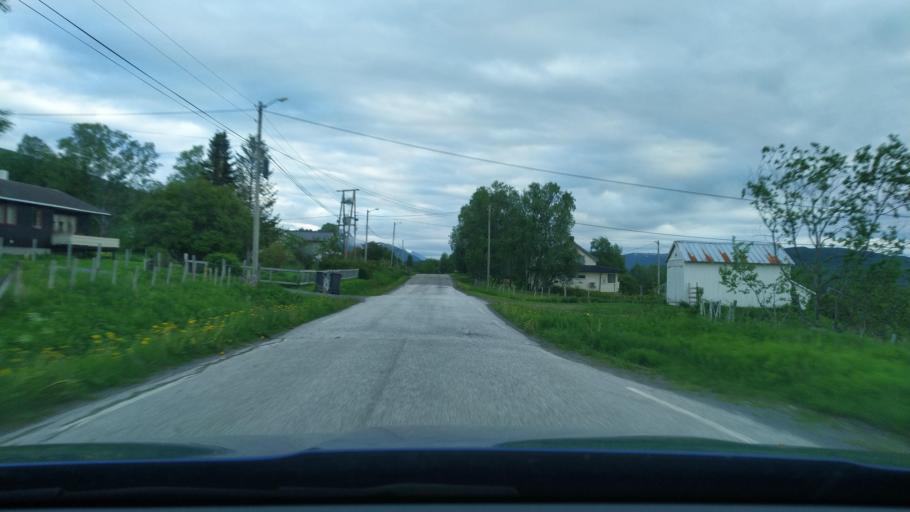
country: NO
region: Troms
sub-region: Tranoy
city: Vangsvika
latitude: 69.1176
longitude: 17.8028
